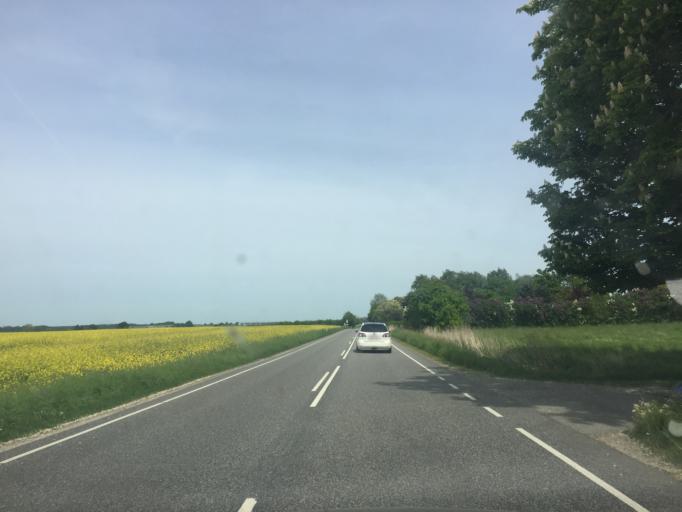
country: DK
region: South Denmark
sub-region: Faaborg-Midtfyn Kommune
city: Ringe
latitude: 55.2113
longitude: 10.5727
